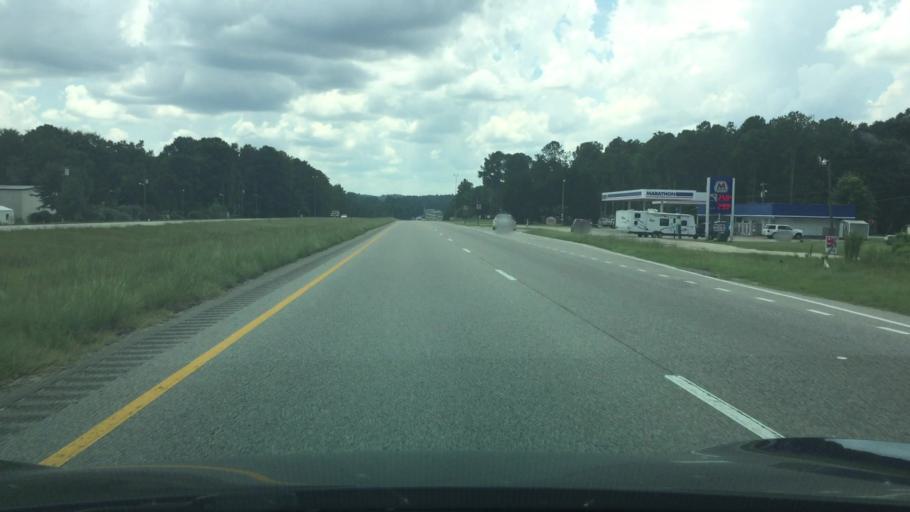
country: US
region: Alabama
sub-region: Pike County
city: Troy
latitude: 31.8571
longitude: -85.9975
